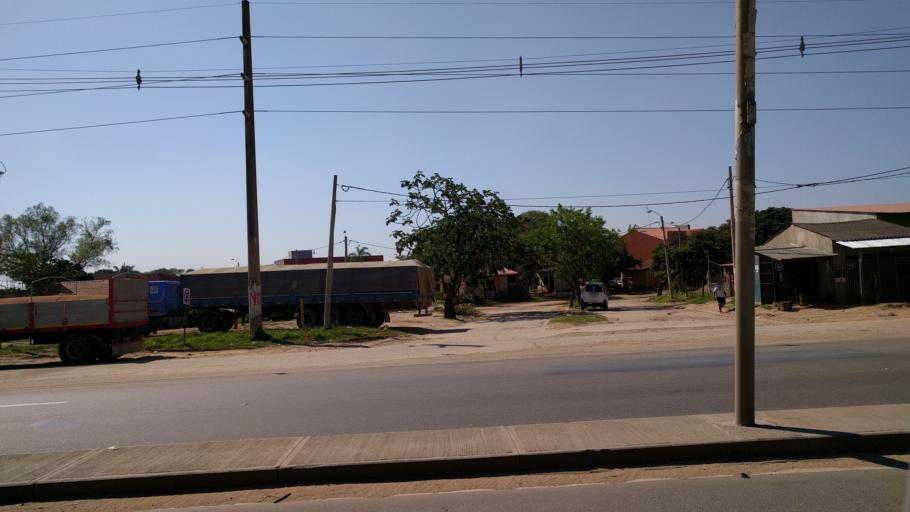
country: BO
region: Santa Cruz
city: Cotoca
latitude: -17.7652
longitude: -63.0887
